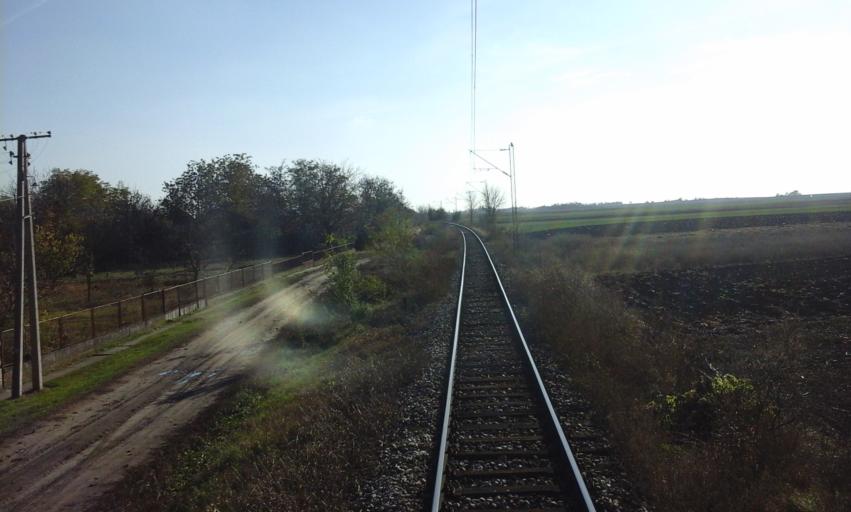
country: RS
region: Autonomna Pokrajina Vojvodina
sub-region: Severnobacki Okrug
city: Backa Topola
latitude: 45.8040
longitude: 19.6474
